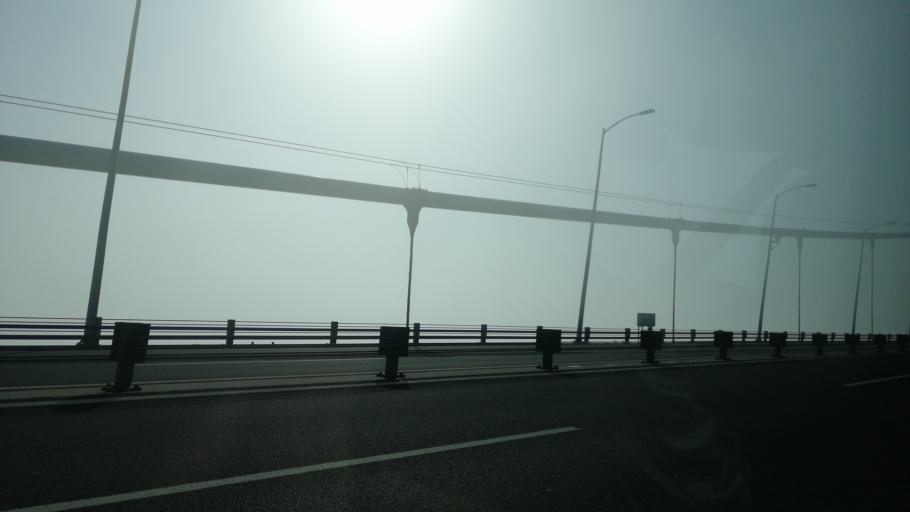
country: TR
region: Kocaeli
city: Tavsancil
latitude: 40.7541
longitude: 29.5156
